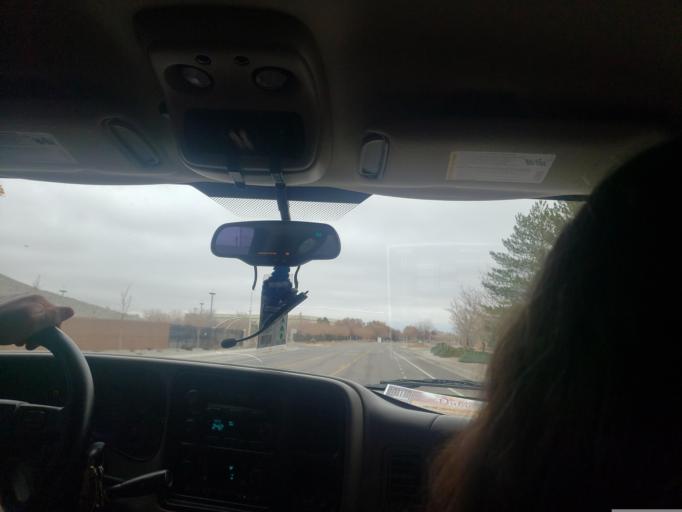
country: US
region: New Mexico
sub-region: Bernalillo County
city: Albuquerque
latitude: 35.0885
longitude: -106.7232
